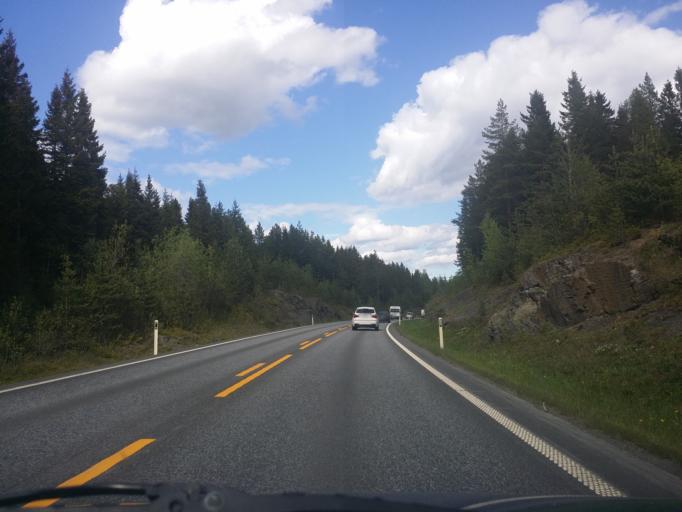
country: NO
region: Oppland
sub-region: Lunner
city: Roa
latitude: 60.2761
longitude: 10.5114
